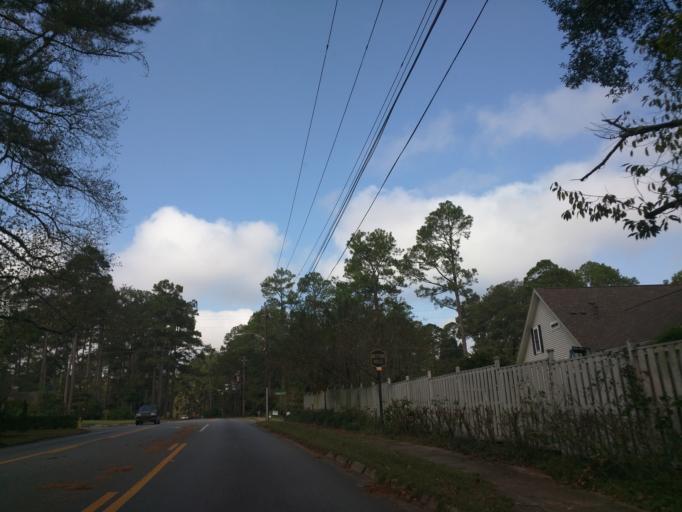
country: US
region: Florida
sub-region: Leon County
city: Tallahassee
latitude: 30.4638
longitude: -84.2607
